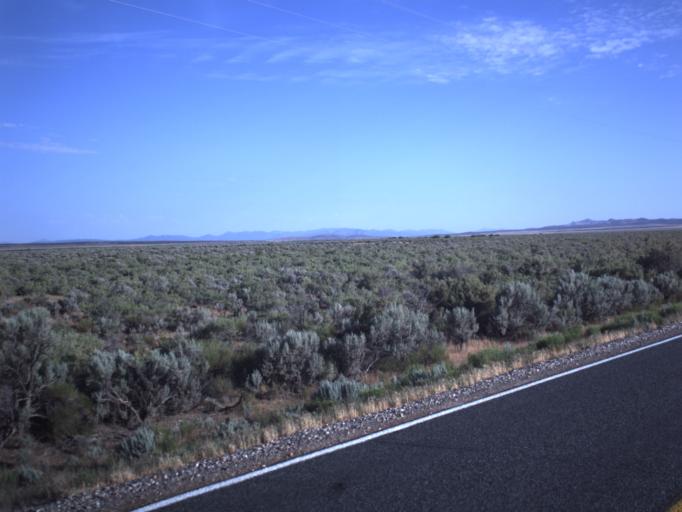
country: US
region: Utah
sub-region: Iron County
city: Enoch
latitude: 37.8148
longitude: -113.0504
